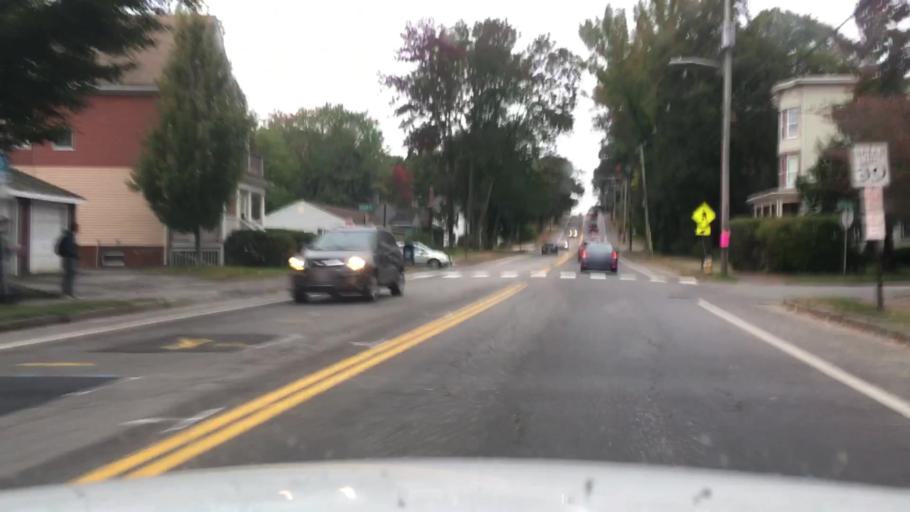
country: US
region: Maine
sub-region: Cumberland County
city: Portland
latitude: 43.6642
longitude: -70.2870
